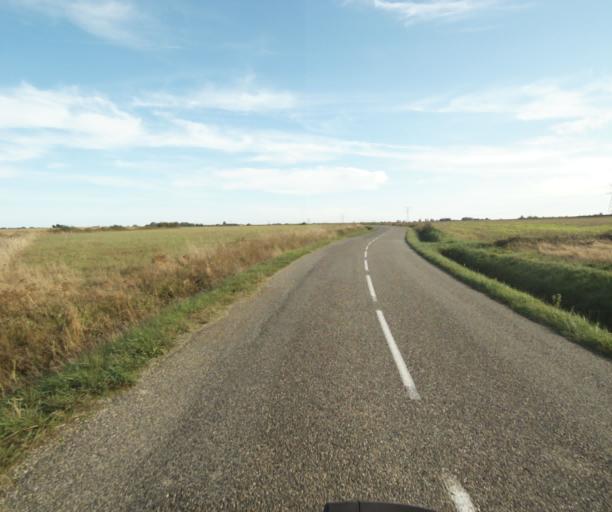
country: FR
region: Midi-Pyrenees
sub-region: Departement du Tarn-et-Garonne
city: Finhan
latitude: 43.9104
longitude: 1.1143
